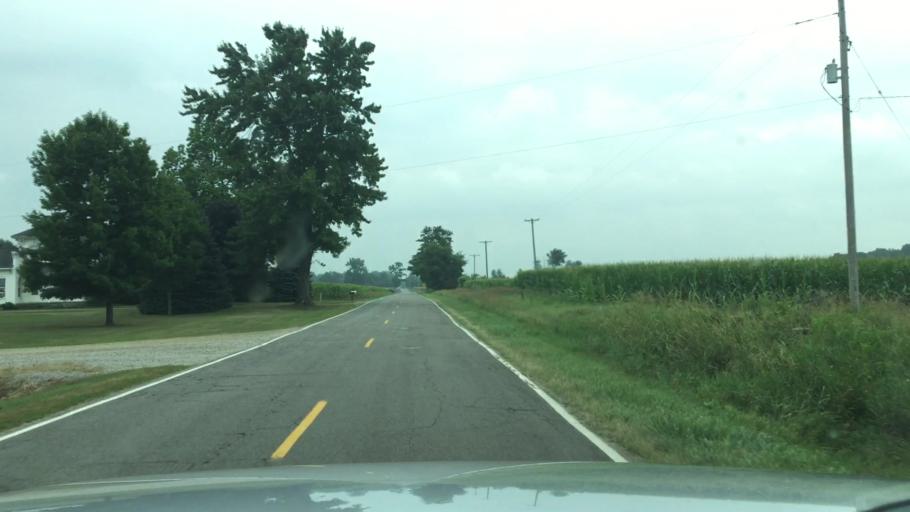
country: US
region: Michigan
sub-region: Shiawassee County
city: New Haven
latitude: 43.0902
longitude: -84.2261
